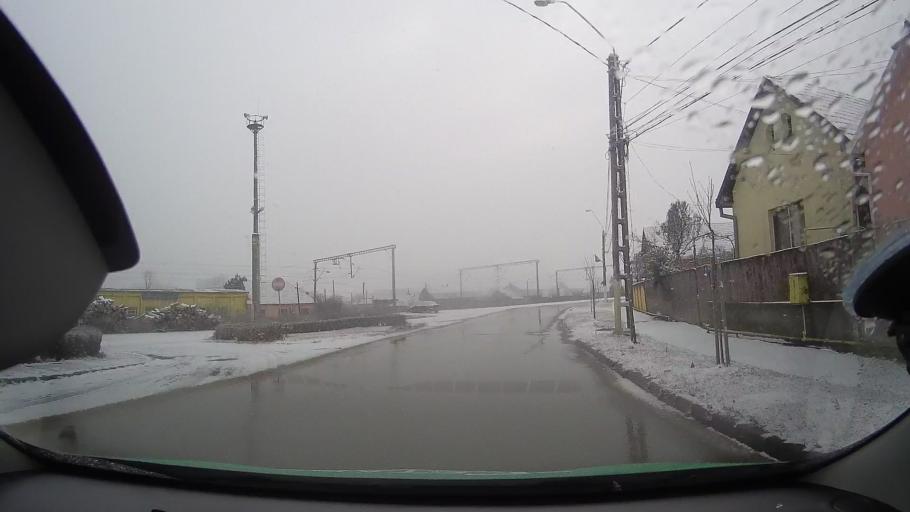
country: RO
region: Alba
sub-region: Municipiul Aiud
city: Aiud
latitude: 46.3102
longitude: 23.7348
